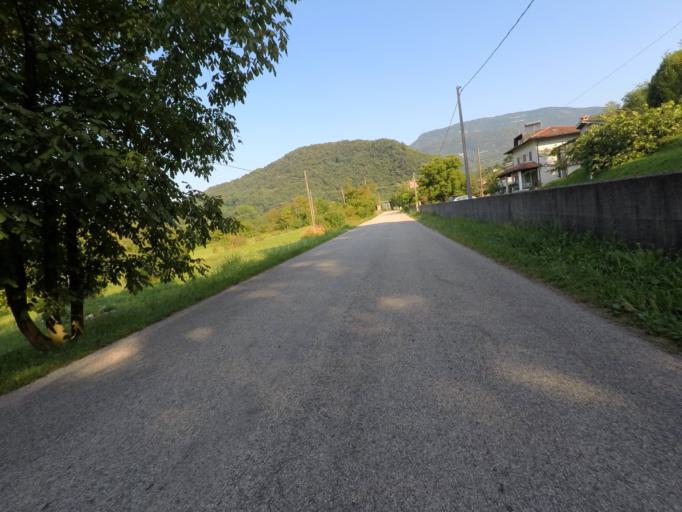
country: IT
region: Friuli Venezia Giulia
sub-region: Provincia di Udine
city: Forgaria nel Friuli
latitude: 46.2073
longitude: 12.9596
